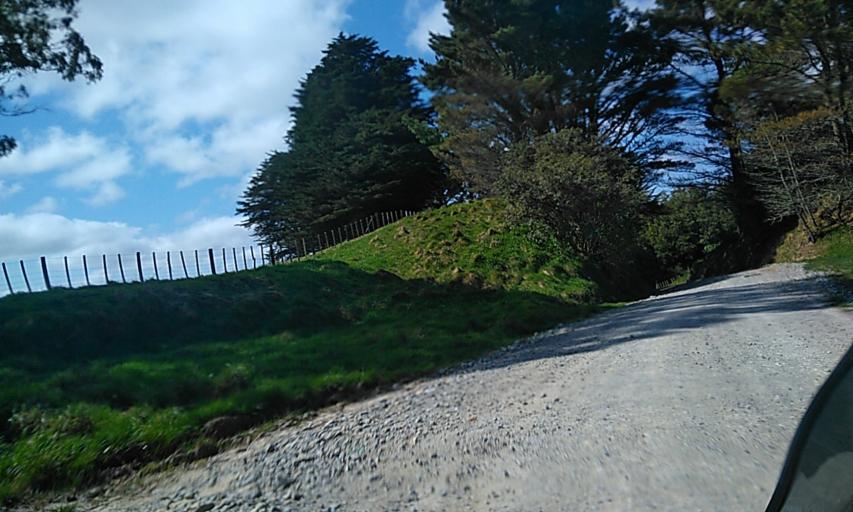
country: NZ
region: Gisborne
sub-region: Gisborne District
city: Gisborne
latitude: -38.1986
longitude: 178.0625
